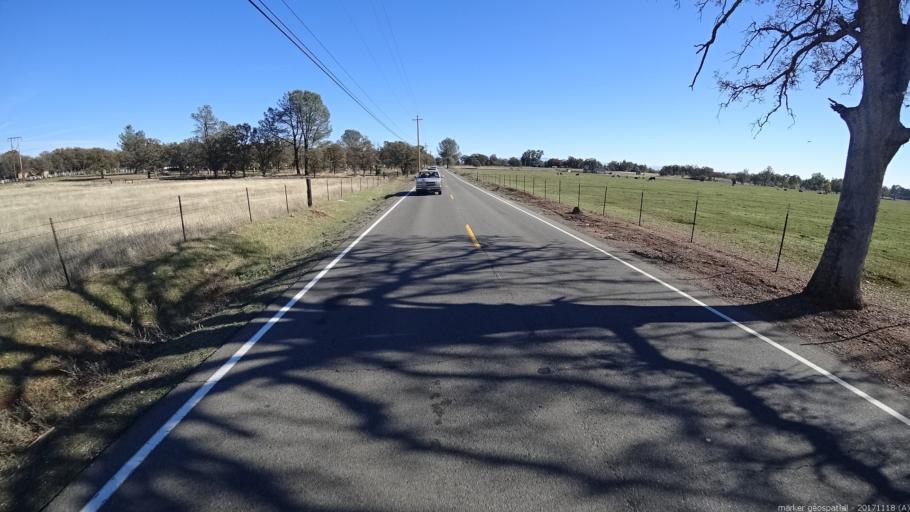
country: US
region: California
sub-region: Shasta County
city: Cottonwood
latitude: 40.3891
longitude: -122.3648
